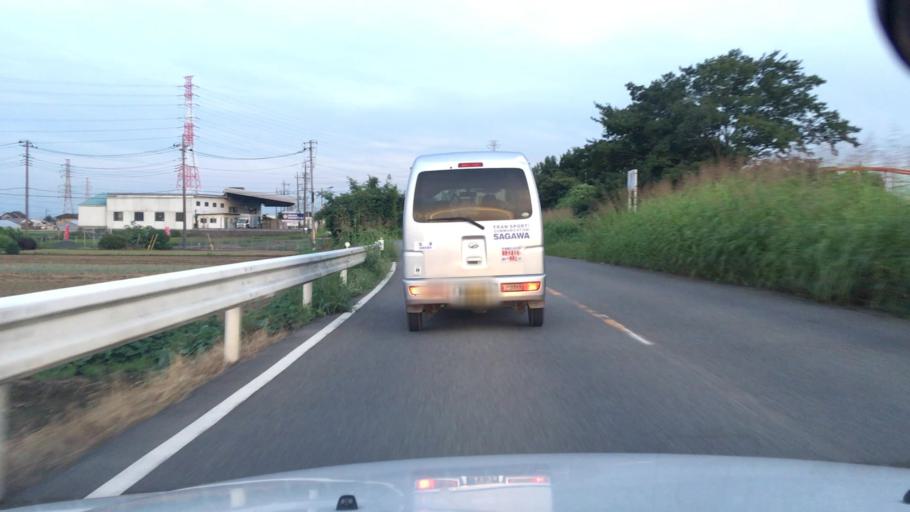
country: JP
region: Saitama
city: Kasukabe
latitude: 35.9390
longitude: 139.7303
